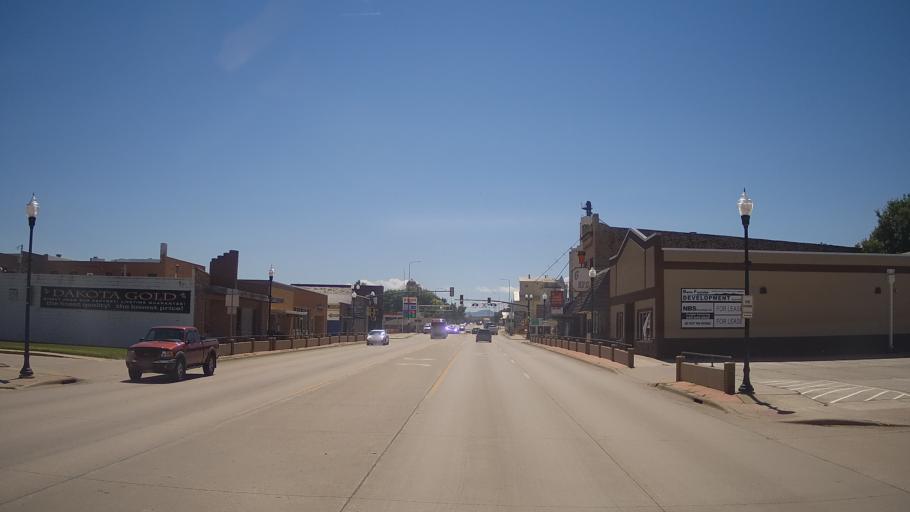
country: US
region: South Dakota
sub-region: Butte County
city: Belle Fourche
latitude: 44.6726
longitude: -103.8536
